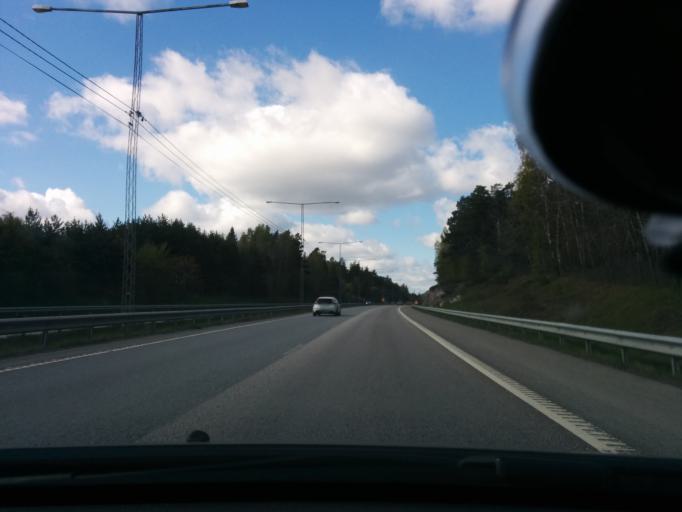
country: SE
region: Stockholm
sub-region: Jarfalla Kommun
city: Jakobsberg
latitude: 59.4340
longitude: 17.8456
